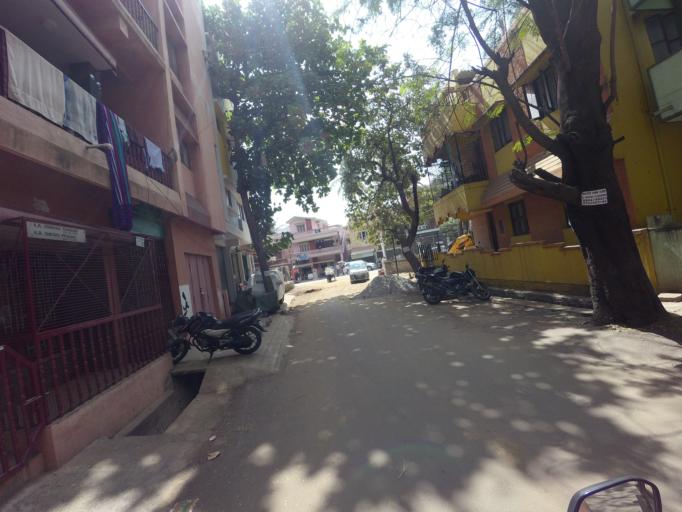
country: IN
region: Karnataka
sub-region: Bangalore Urban
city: Bangalore
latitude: 12.9582
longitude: 77.5374
